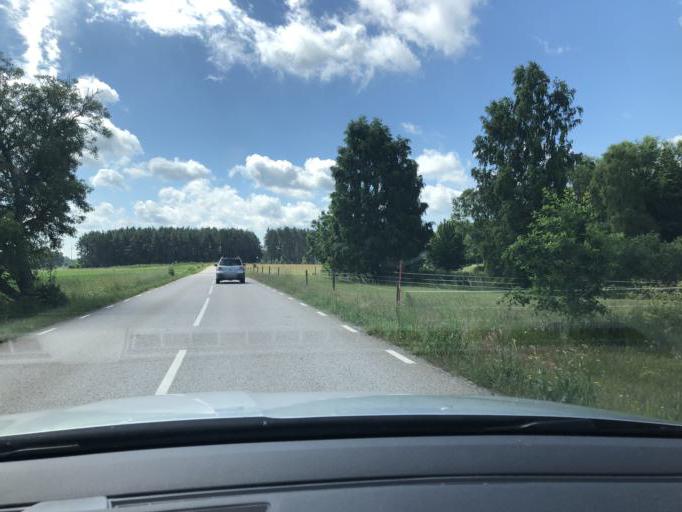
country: SE
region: Blekinge
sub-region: Solvesborgs Kommun
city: Soelvesborg
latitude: 56.0820
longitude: 14.6075
